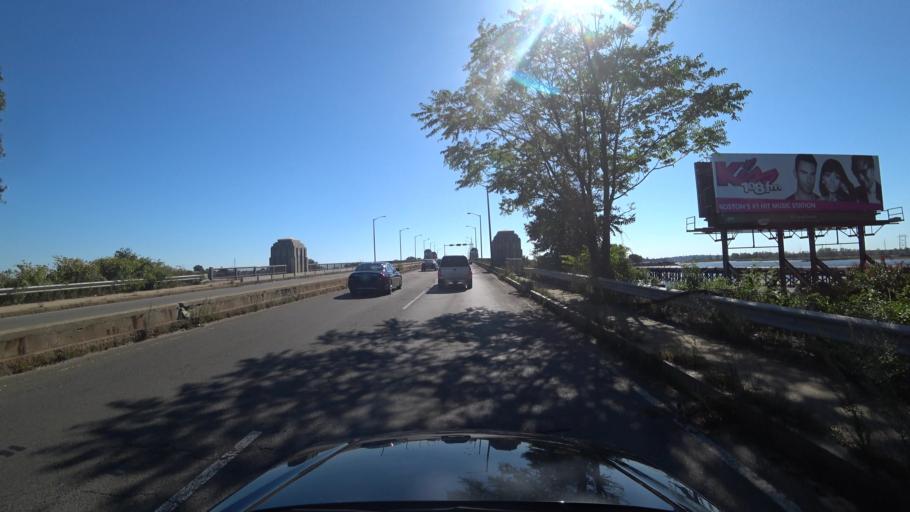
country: US
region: Massachusetts
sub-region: Essex County
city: Lynn
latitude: 42.4458
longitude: -70.9654
